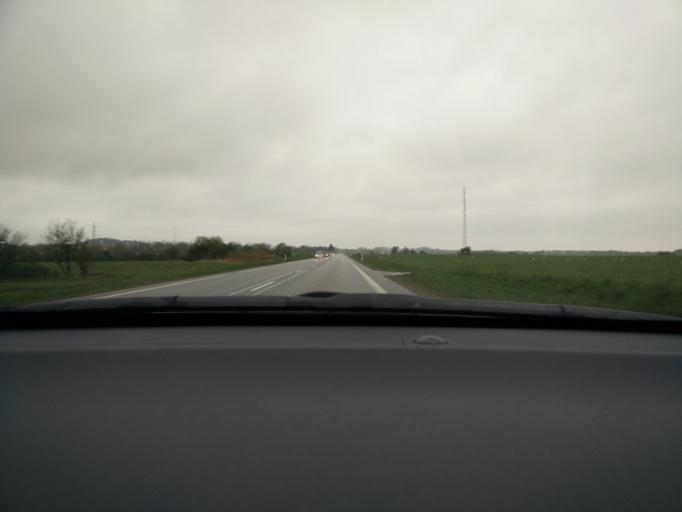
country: DK
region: Central Jutland
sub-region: Viborg Kommune
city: Stoholm
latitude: 56.5342
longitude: 9.1790
